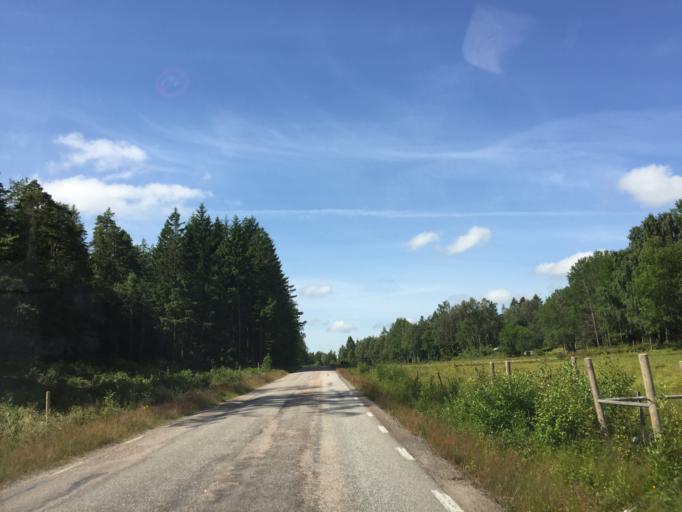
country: SE
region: Vaestra Goetaland
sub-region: Orust
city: Henan
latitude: 58.2933
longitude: 11.6532
